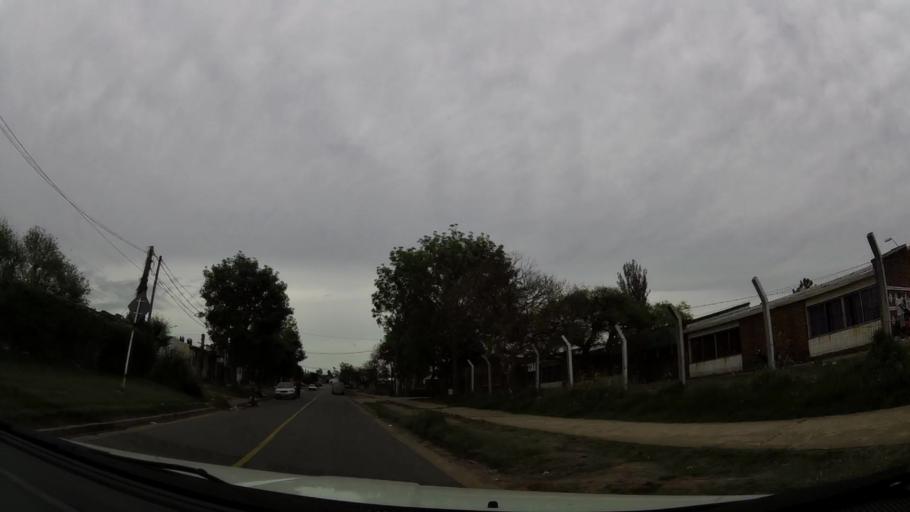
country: UY
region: Maldonado
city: Maldonado
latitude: -34.8797
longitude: -54.9795
